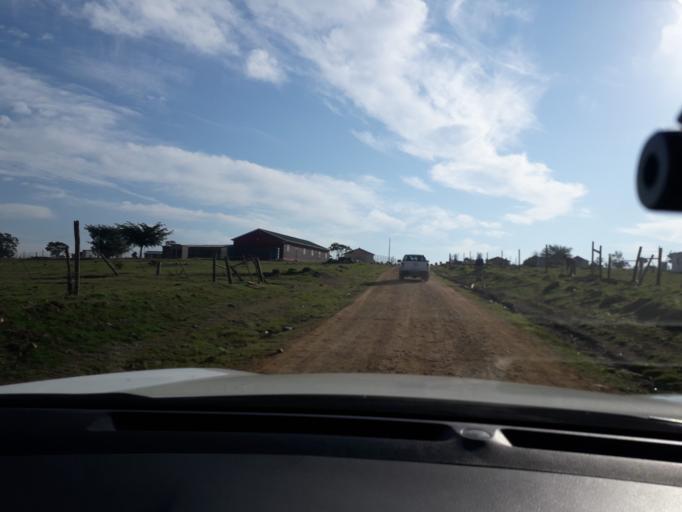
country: ZA
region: Eastern Cape
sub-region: Buffalo City Metropolitan Municipality
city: Bhisho
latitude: -32.9389
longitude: 27.2901
